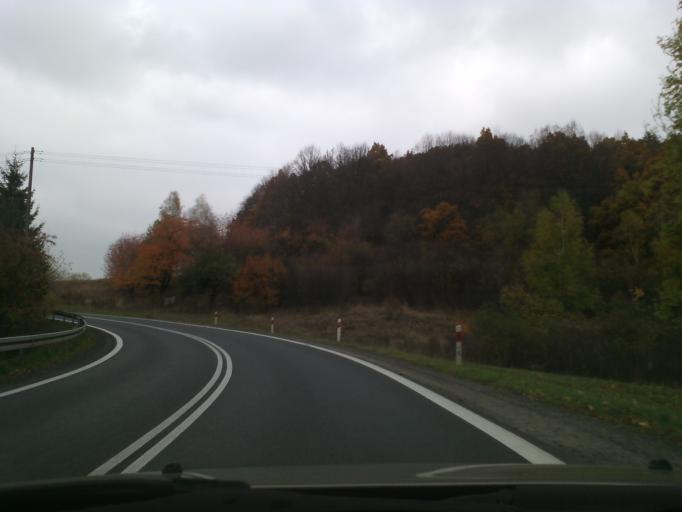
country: PL
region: Lower Silesian Voivodeship
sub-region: Powiat jaworski
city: Bolkow
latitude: 50.9355
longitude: 16.0721
